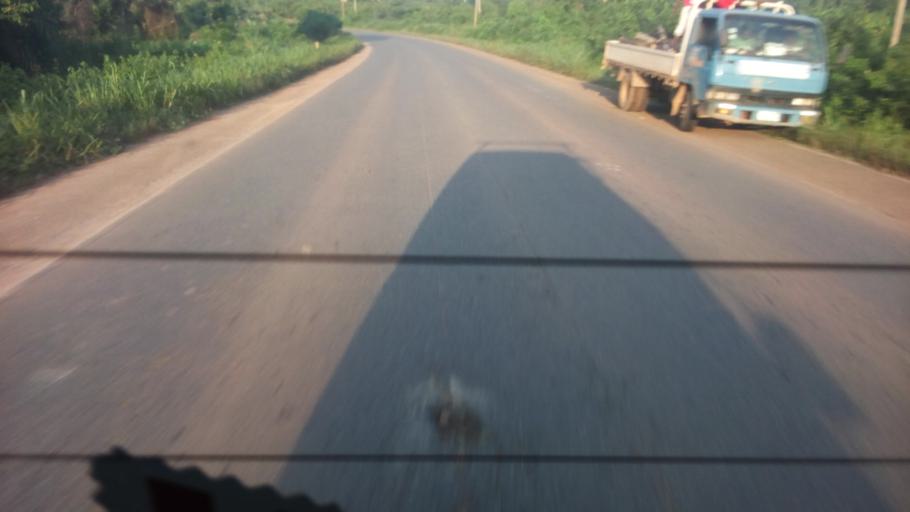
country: GH
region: Western
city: Tarkwa
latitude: 5.1706
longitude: -2.0579
